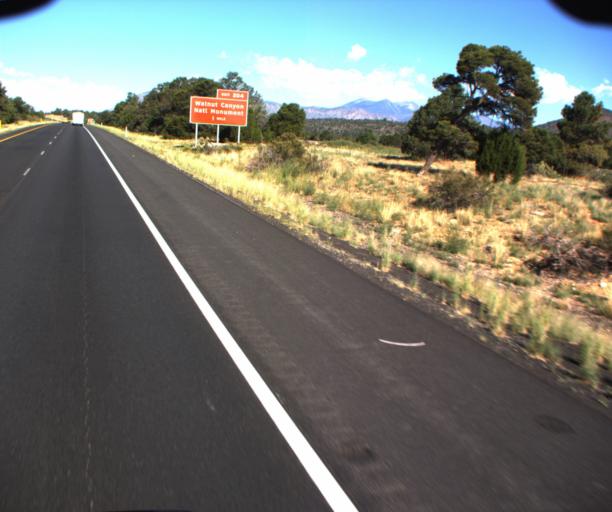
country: US
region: Arizona
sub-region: Coconino County
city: Flagstaff
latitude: 35.2053
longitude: -111.4948
